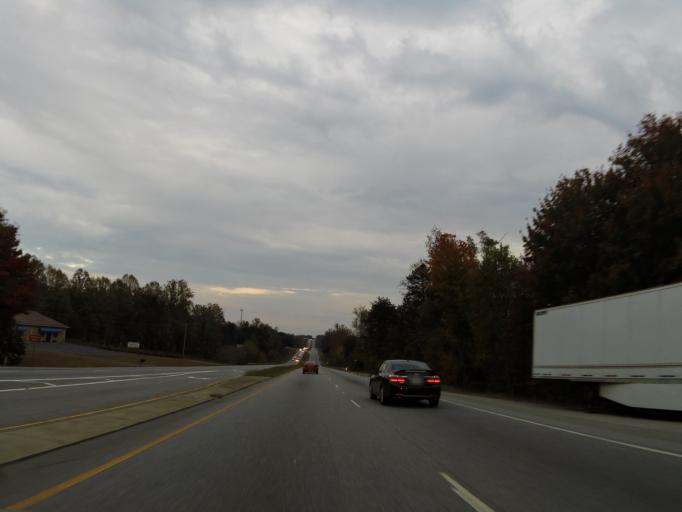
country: US
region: North Carolina
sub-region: Caldwell County
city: Sawmills
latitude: 35.8283
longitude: -81.4521
